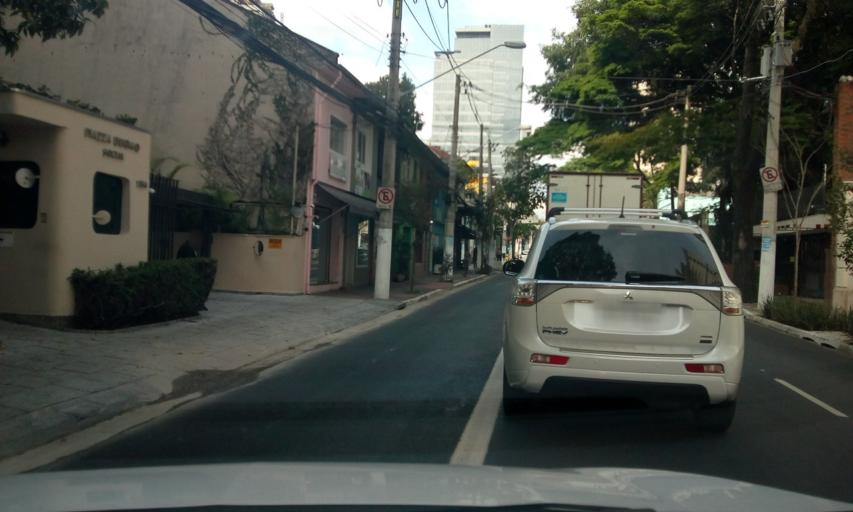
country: BR
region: Sao Paulo
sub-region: Sao Paulo
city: Sao Paulo
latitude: -23.5858
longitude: -46.6855
